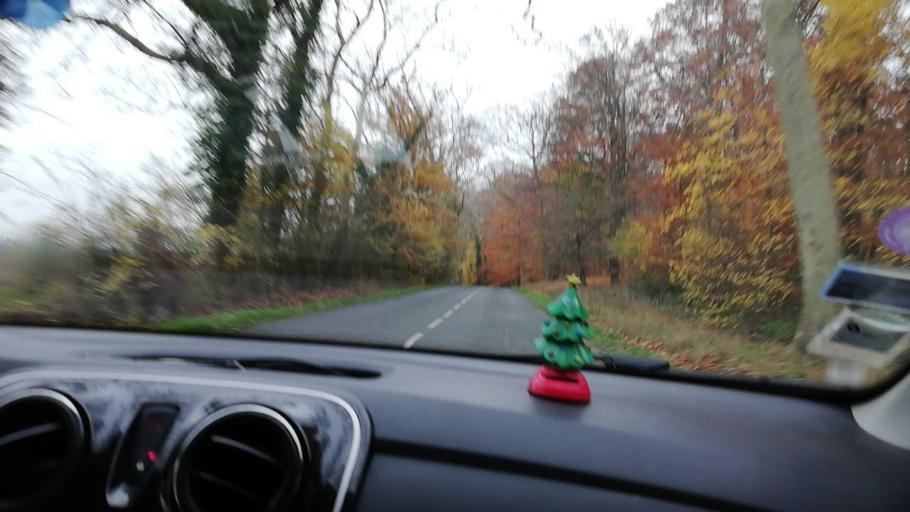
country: FR
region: Picardie
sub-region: Departement de l'Oise
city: Lagny-le-Sec
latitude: 49.0407
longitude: 2.7466
